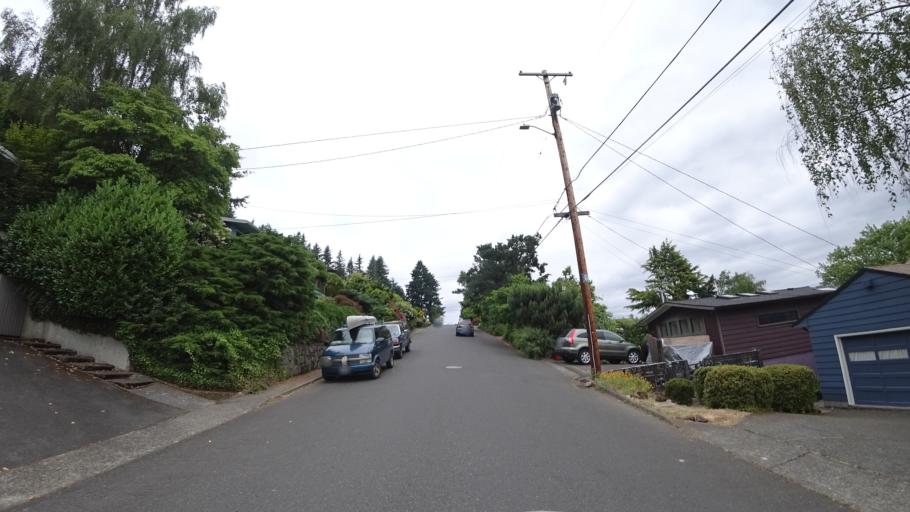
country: US
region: Oregon
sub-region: Multnomah County
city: Lents
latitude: 45.5110
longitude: -122.5890
